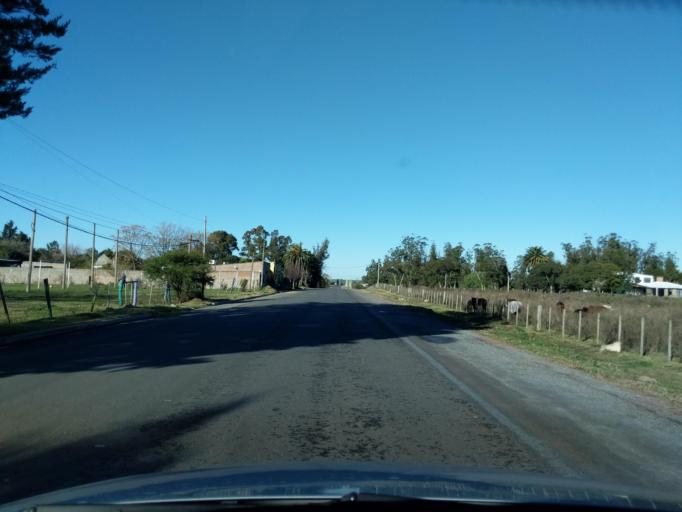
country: UY
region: Florida
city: Florida
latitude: -34.0932
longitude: -56.2392
